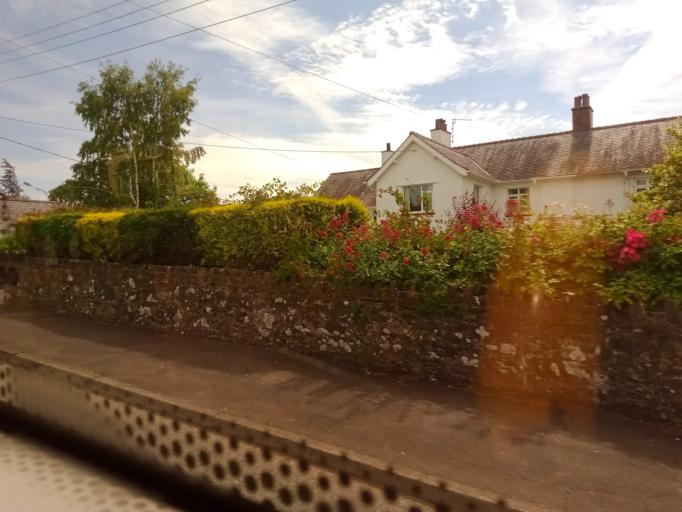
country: GB
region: Wales
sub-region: Anglesey
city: Menai Bridge
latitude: 53.2362
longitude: -4.1558
